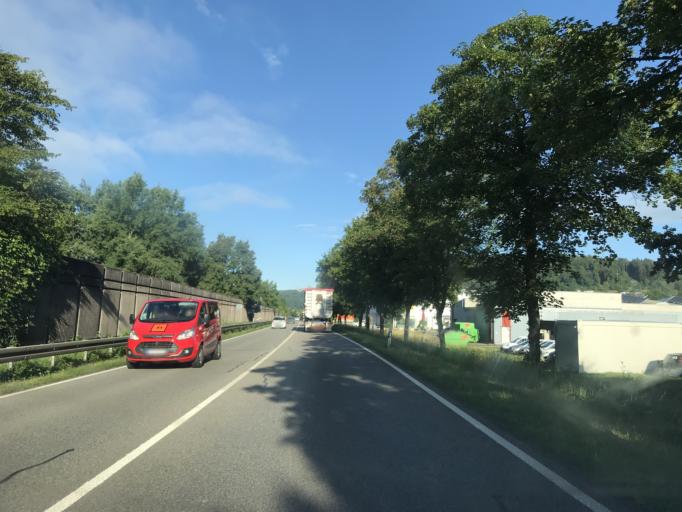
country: DE
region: Baden-Wuerttemberg
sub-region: Freiburg Region
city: Steinen
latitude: 47.6405
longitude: 7.7026
